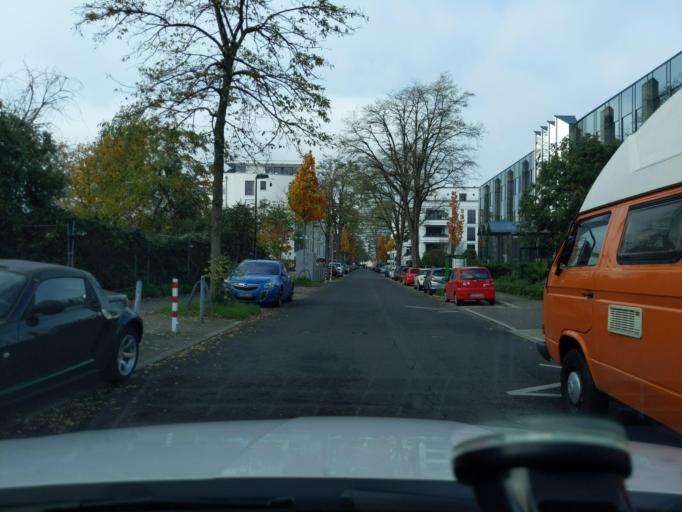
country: DE
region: North Rhine-Westphalia
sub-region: Regierungsbezirk Dusseldorf
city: Dusseldorf
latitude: 51.2331
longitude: 6.7397
